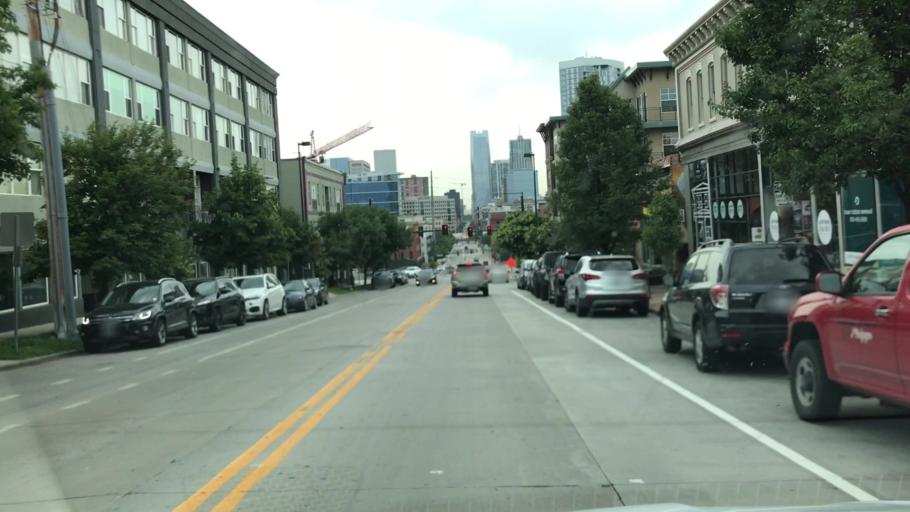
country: US
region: Colorado
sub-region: Denver County
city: Denver
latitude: 39.7581
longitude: -105.0115
